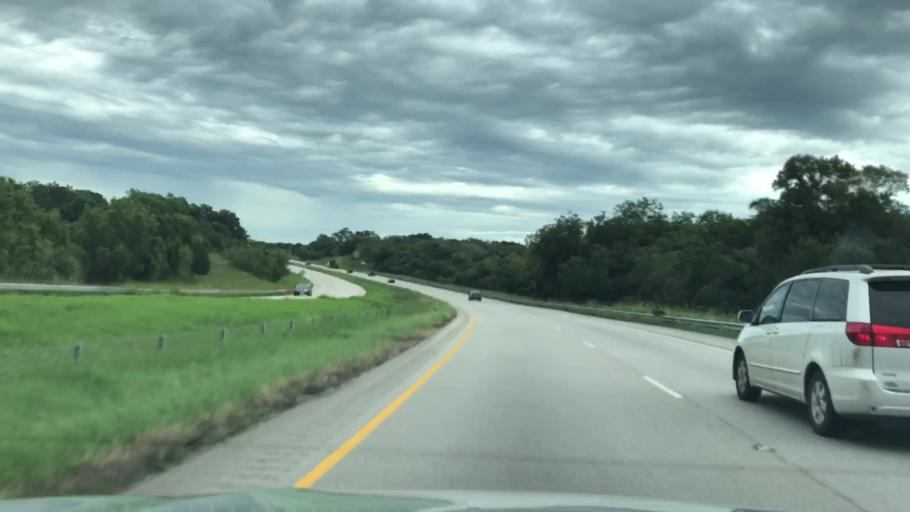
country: US
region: Texas
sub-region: Colorado County
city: Weimar
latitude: 29.6883
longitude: -96.8339
